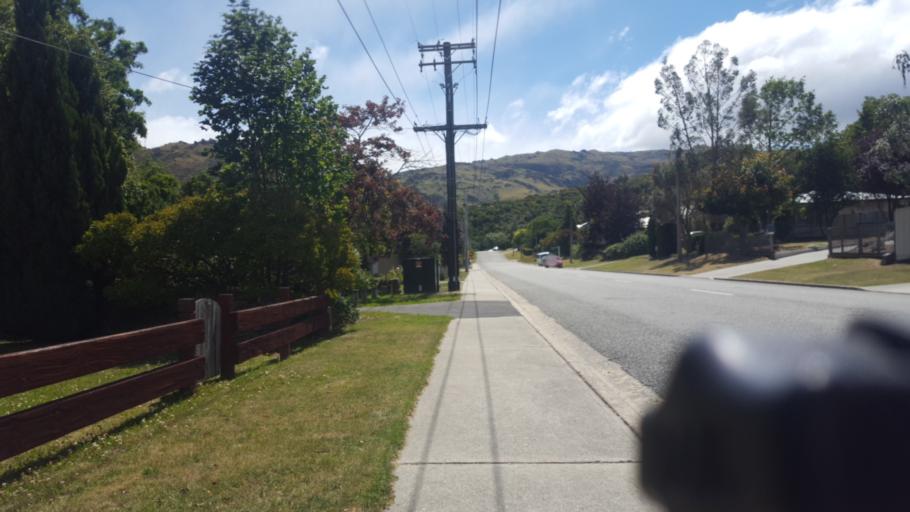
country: NZ
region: Otago
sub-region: Queenstown-Lakes District
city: Wanaka
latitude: -45.1865
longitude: 169.3206
